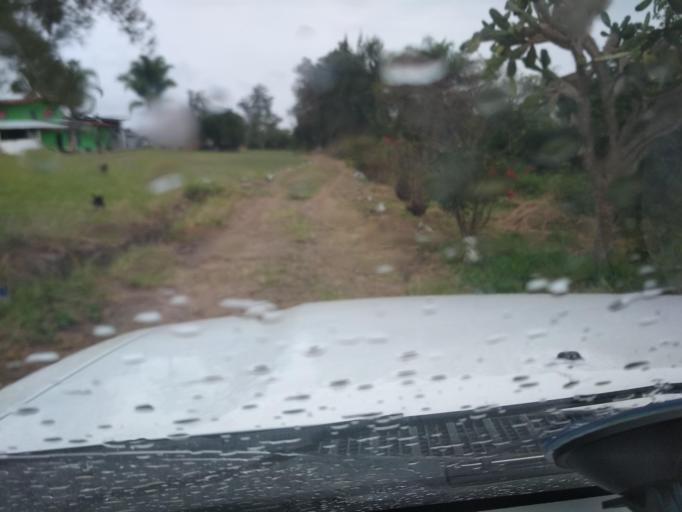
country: MX
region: Veracruz
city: El Castillo
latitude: 19.5346
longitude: -96.8224
